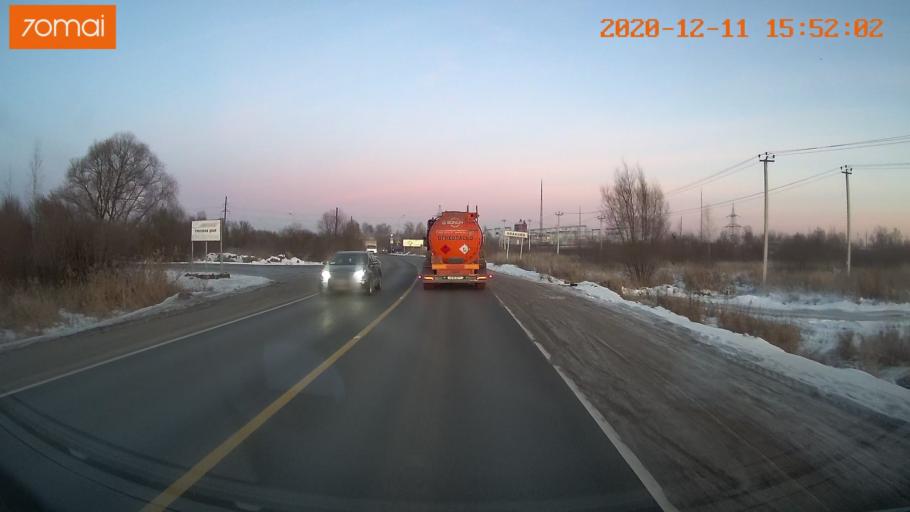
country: RU
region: Ivanovo
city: Novo-Talitsy
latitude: 56.9873
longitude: 40.9018
